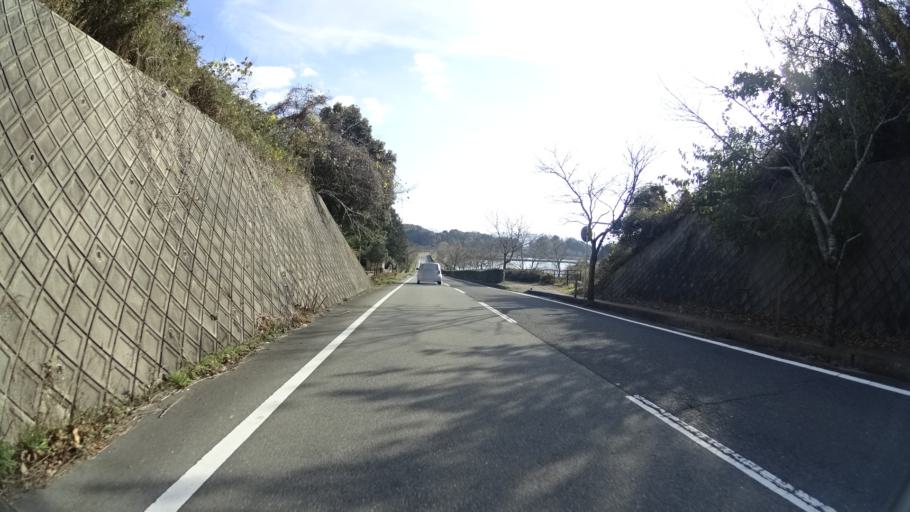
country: JP
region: Kyoto
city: Kameoka
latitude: 35.0703
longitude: 135.5665
